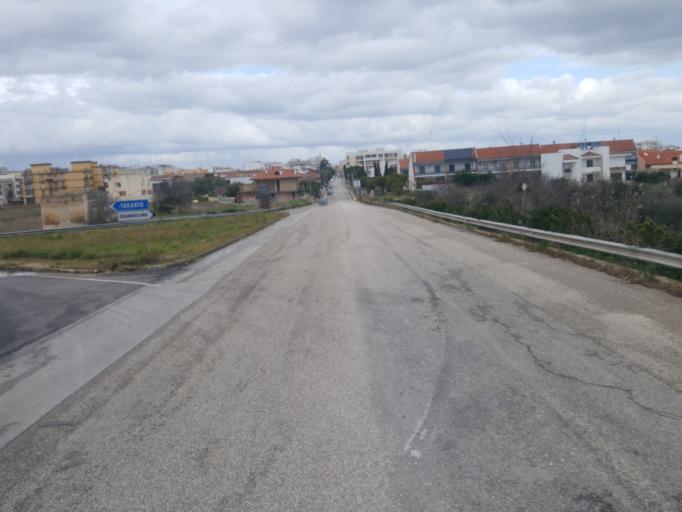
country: IT
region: Apulia
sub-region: Provincia di Bari
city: Casamassima
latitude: 40.9496
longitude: 16.9307
